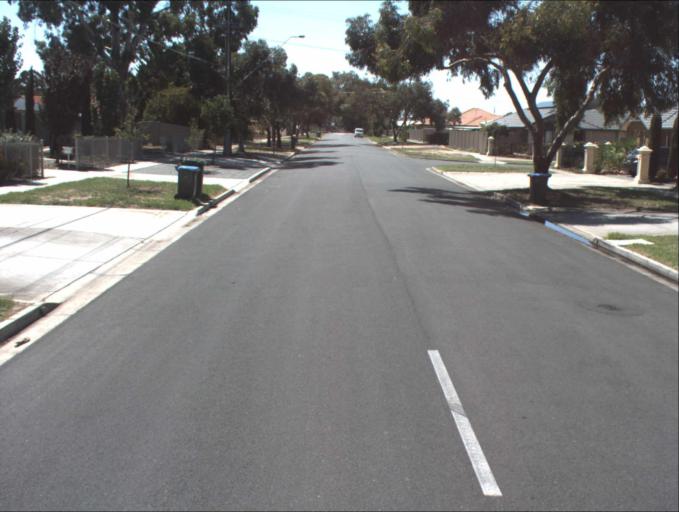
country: AU
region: South Australia
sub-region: Charles Sturt
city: Woodville North
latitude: -34.8615
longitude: 138.5608
